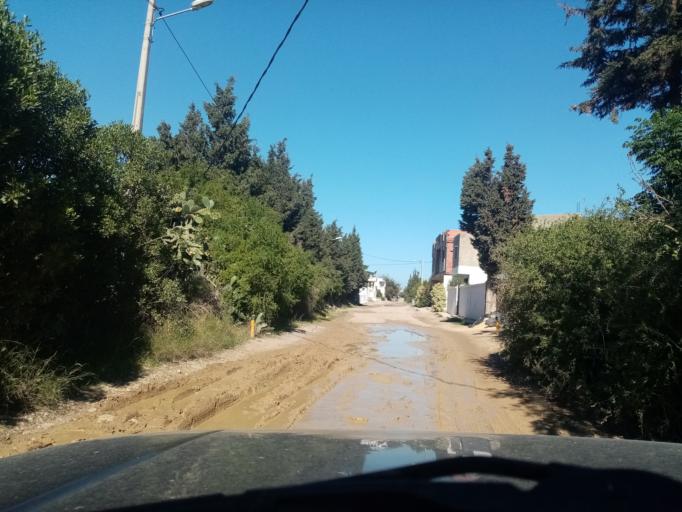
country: TN
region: Nabul
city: Bu `Urqub
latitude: 36.5753
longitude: 10.5726
